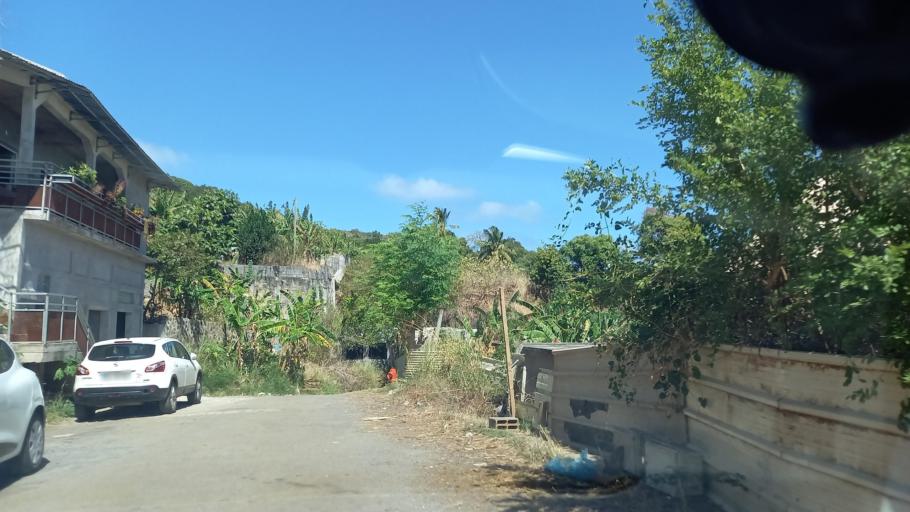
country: YT
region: Kani-Keli
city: Kani Keli
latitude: -12.9654
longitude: 45.1130
